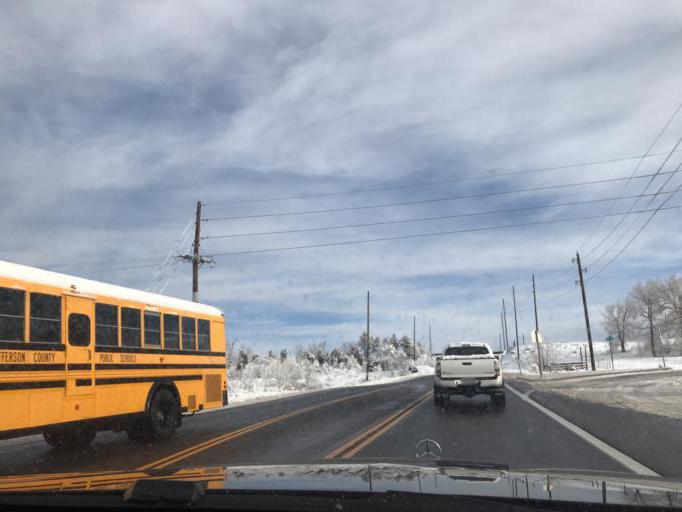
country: US
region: Colorado
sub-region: Jefferson County
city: Applewood
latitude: 39.8448
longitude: -105.1653
